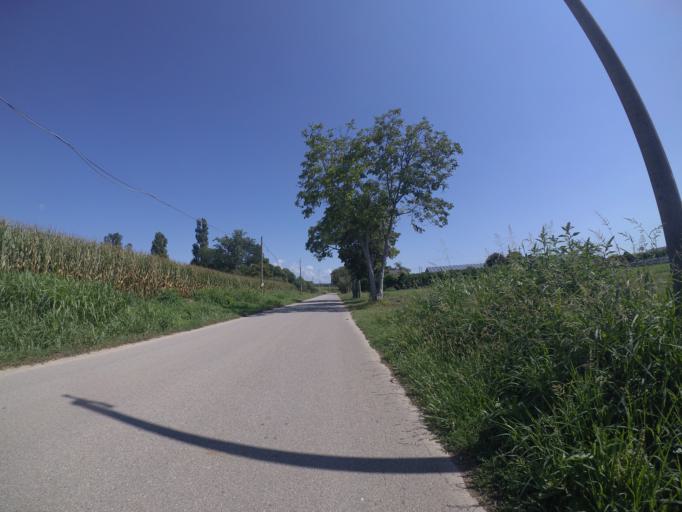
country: IT
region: Friuli Venezia Giulia
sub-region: Provincia di Udine
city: Lestizza
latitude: 45.9793
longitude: 13.1401
